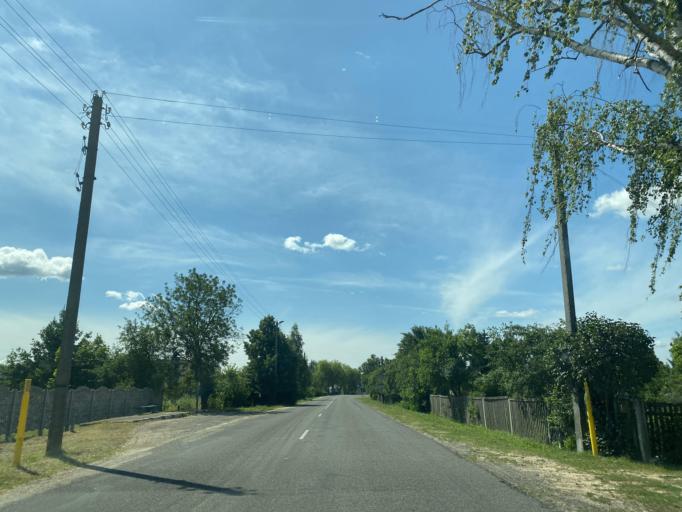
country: BY
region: Brest
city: Ivanava
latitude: 52.1878
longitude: 25.6095
